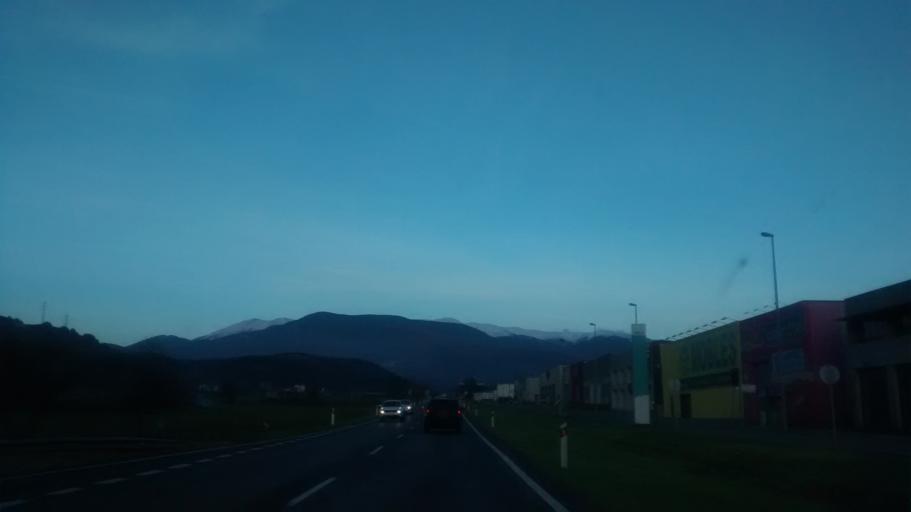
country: ES
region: Catalonia
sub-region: Provincia de Lleida
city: la Seu d'Urgell
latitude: 42.3378
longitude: 1.4156
